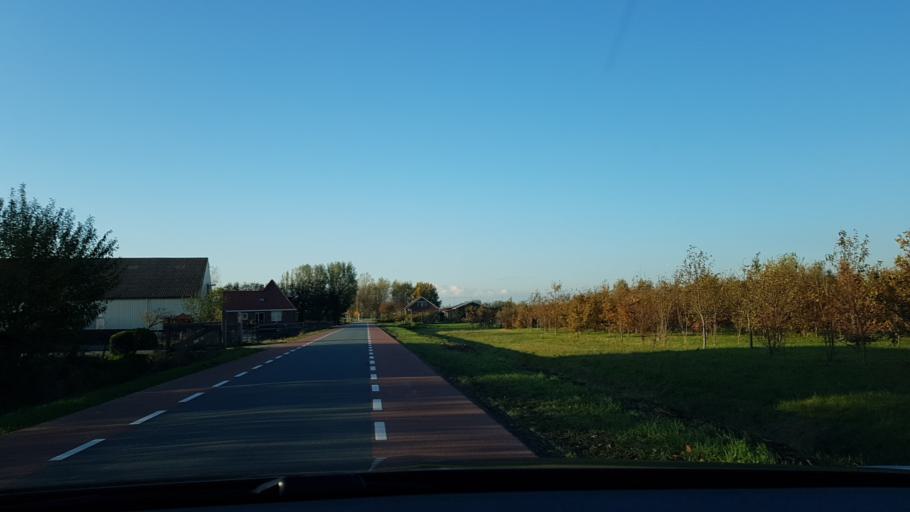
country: NL
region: North Holland
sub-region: Gemeente Beverwijk
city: Beverwijk
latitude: 52.4724
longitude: 4.6878
